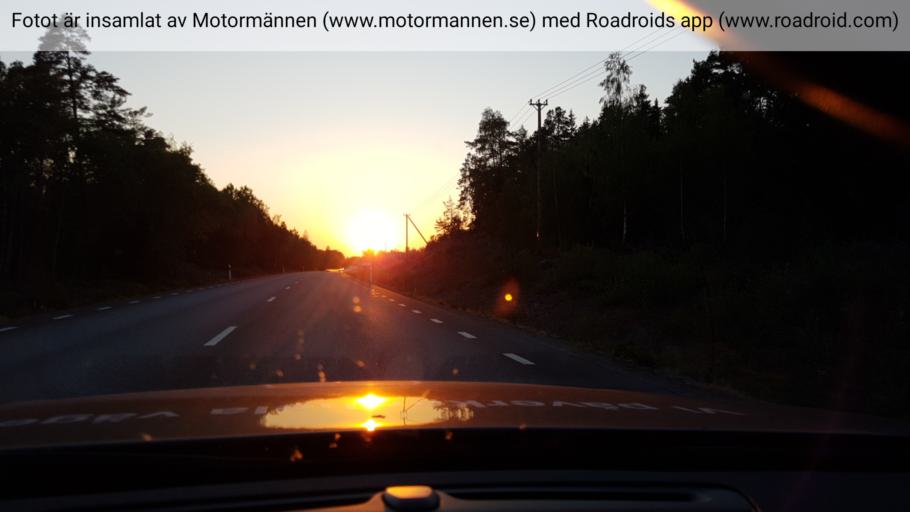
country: SE
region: Uppsala
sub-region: Osthammars Kommun
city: Bjorklinge
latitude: 59.9710
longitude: 17.3677
